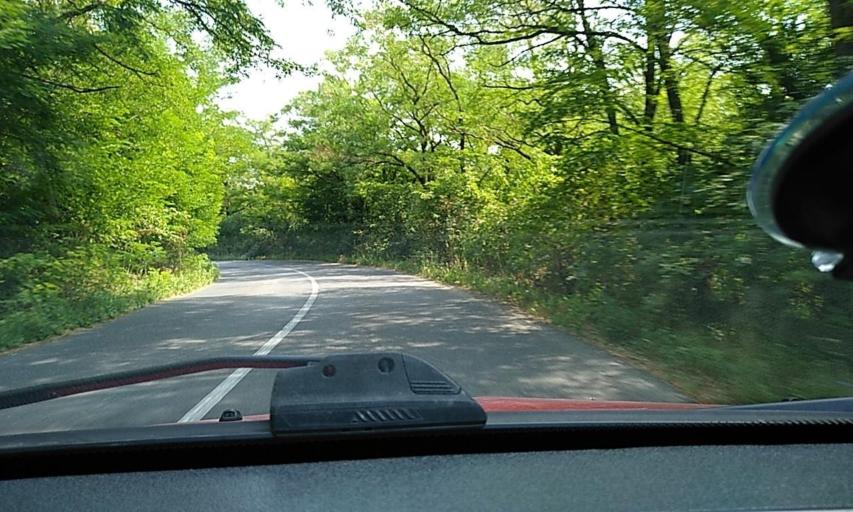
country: RO
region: Brasov
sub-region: Oras Rupea
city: Rupea
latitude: 46.0230
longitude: 25.1970
